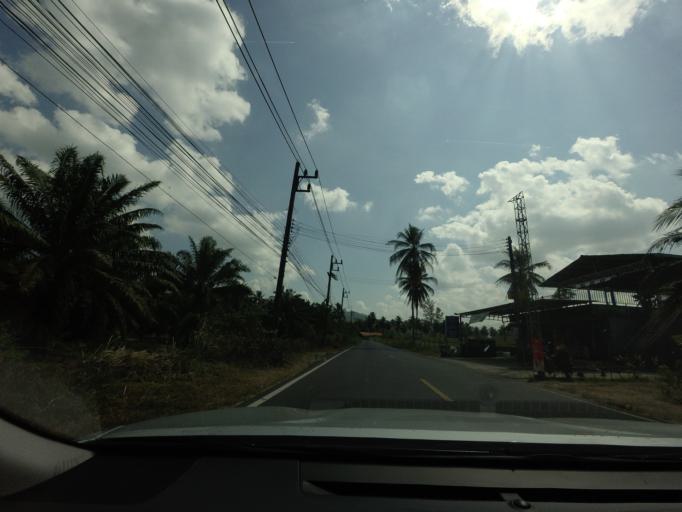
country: TH
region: Phangnga
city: Ban Khao Lak
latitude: 8.7238
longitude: 98.2448
